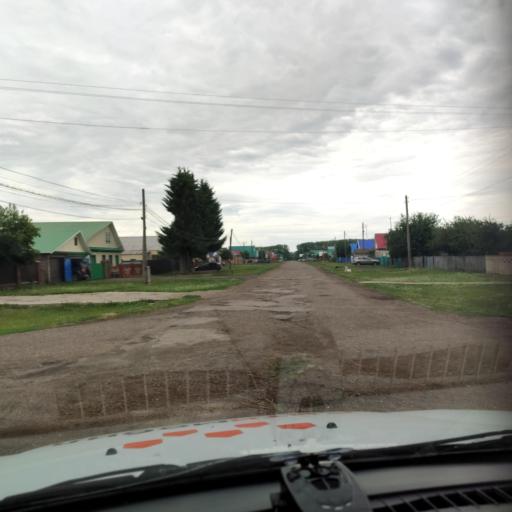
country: RU
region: Bashkortostan
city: Kabakovo
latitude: 54.4559
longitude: 55.9542
